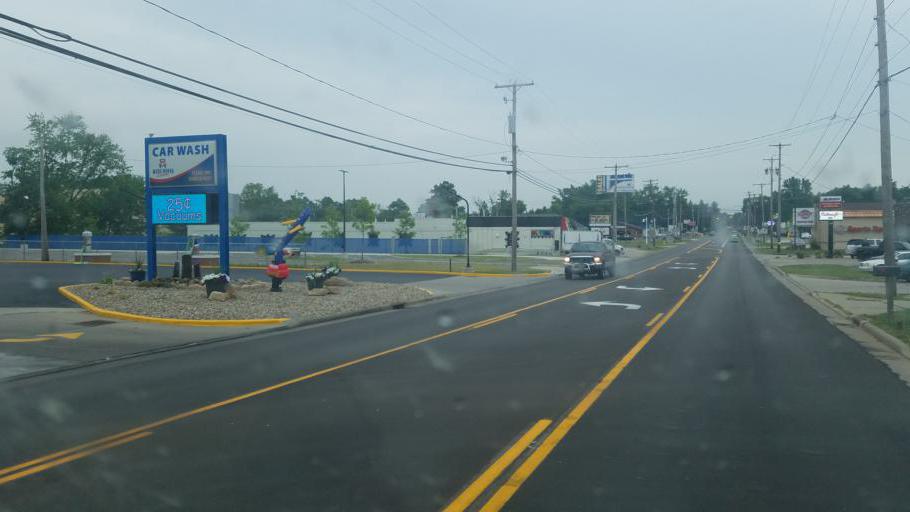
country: US
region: Ohio
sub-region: Summit County
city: Portage Lakes
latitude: 41.0077
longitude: -81.5555
